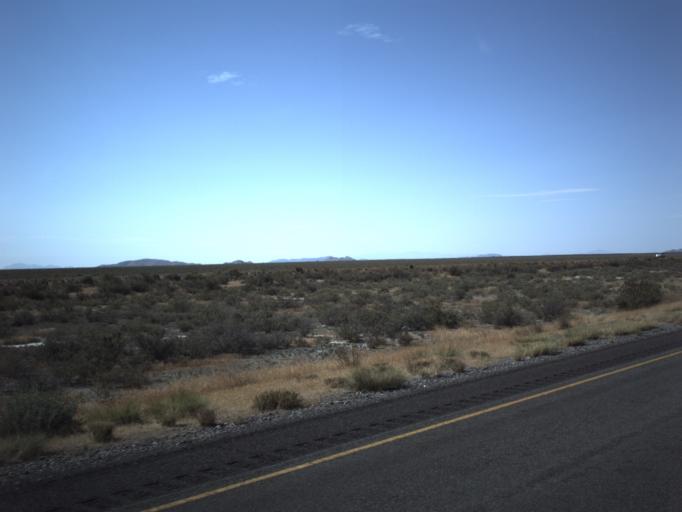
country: US
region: Utah
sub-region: Tooele County
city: Grantsville
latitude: 40.7420
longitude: -113.0792
